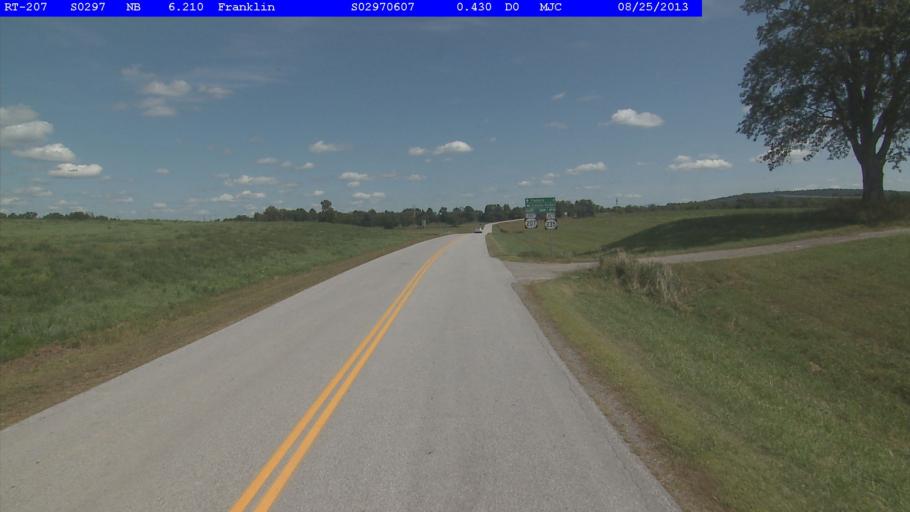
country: CA
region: Quebec
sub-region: Monteregie
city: Bedford
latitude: 45.0068
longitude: -72.9824
